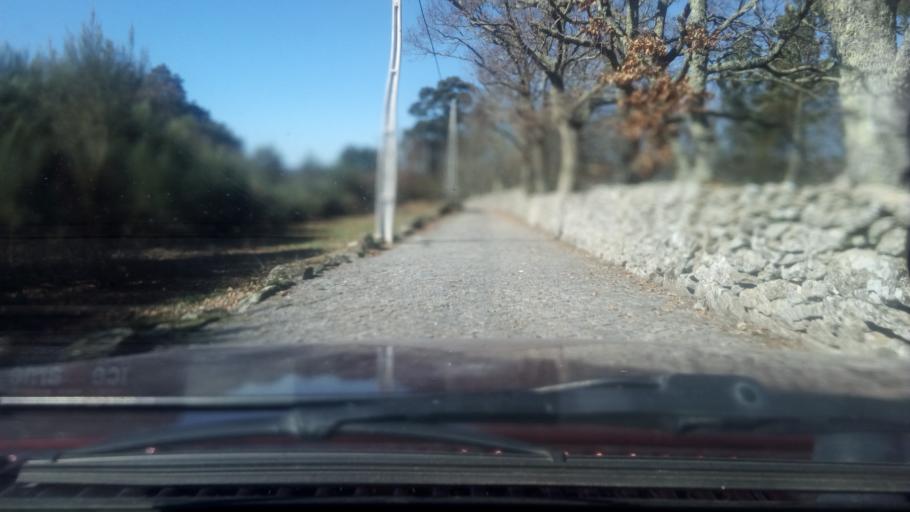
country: PT
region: Guarda
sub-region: Fornos de Algodres
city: Fornos de Algodres
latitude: 40.6088
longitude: -7.5021
